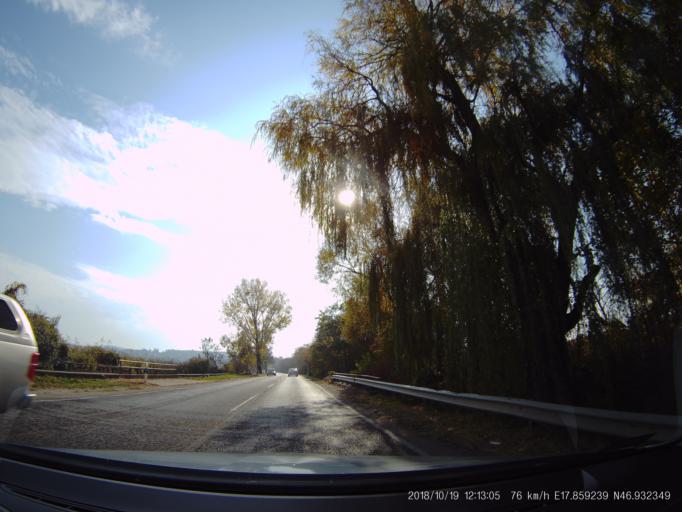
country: HU
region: Veszprem
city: Balatonfured
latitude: 46.9323
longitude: 17.8592
